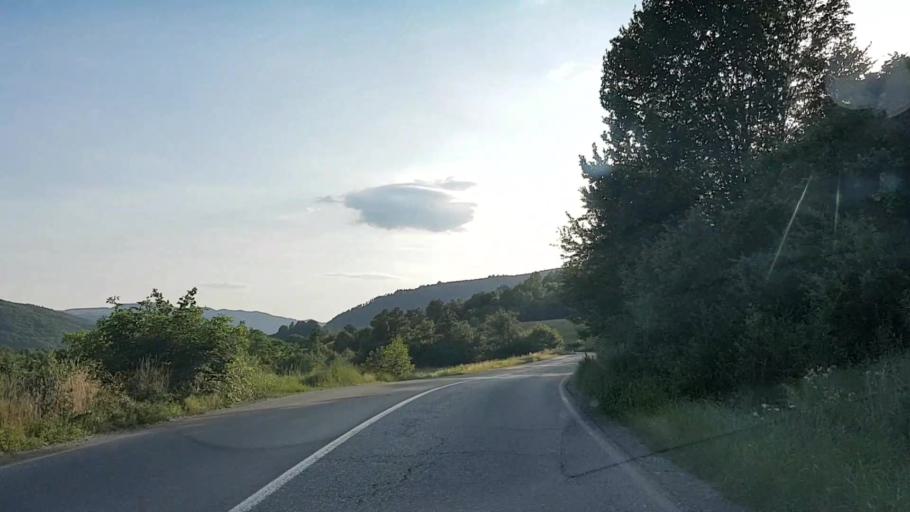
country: RO
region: Harghita
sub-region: Comuna Praid
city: Praid
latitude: 46.5702
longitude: 25.1742
